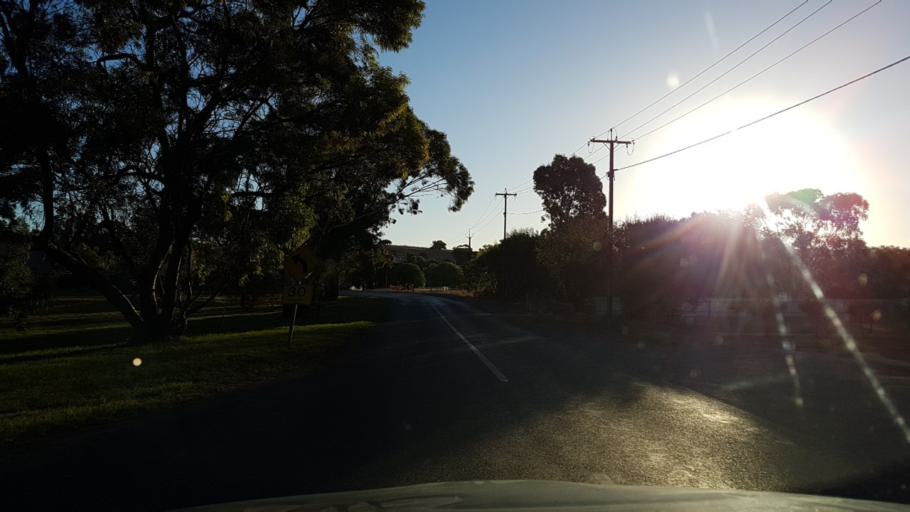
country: AU
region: South Australia
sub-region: Clare and Gilbert Valleys
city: Clare
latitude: -34.0228
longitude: 138.6891
